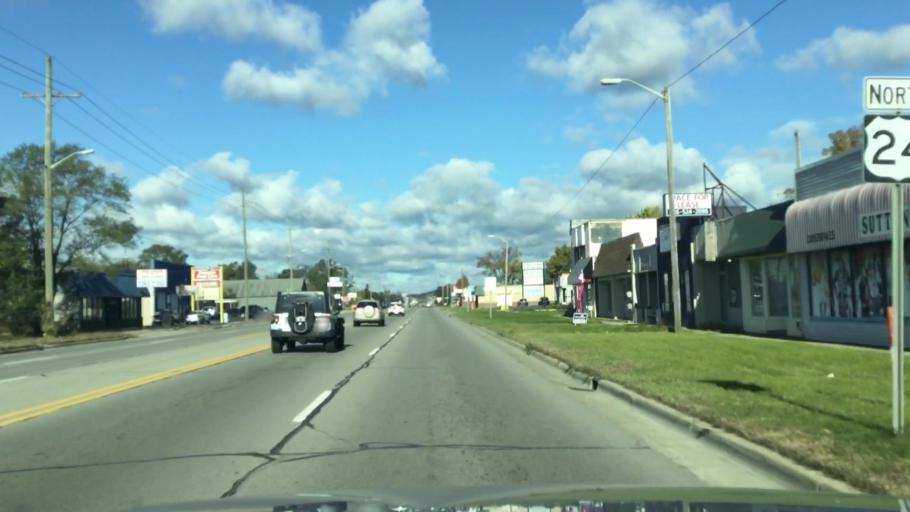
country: US
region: Michigan
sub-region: Oakland County
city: Waterford
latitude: 42.6843
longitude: -83.3777
